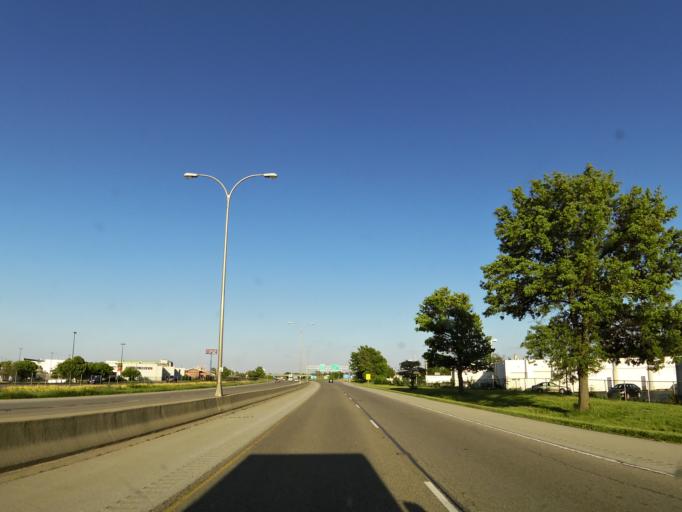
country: US
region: Illinois
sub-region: Champaign County
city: Champaign
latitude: 40.1363
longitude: -88.2657
